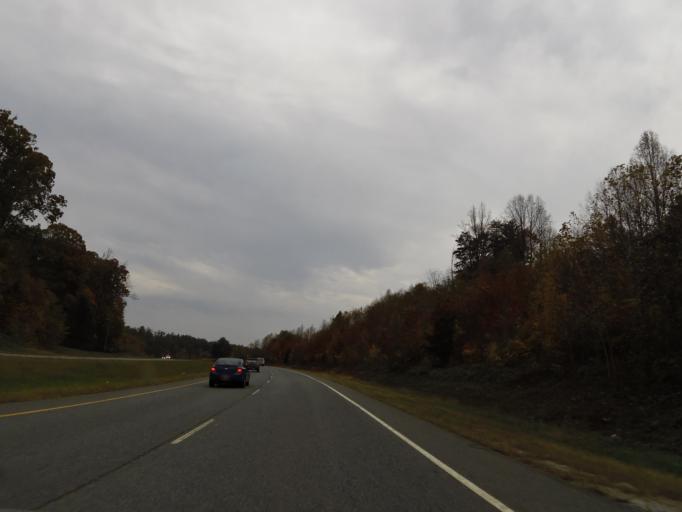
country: US
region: North Carolina
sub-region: Caldwell County
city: Lenoir
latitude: 35.9915
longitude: -81.5726
